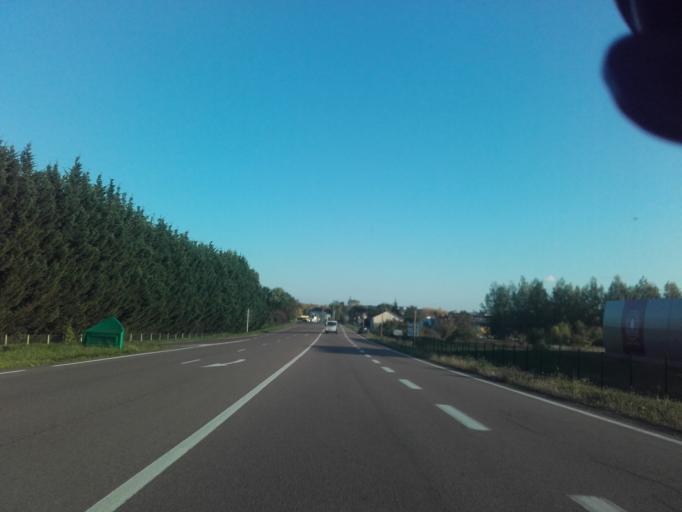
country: FR
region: Bourgogne
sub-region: Departement de la Cote-d'Or
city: Corpeau
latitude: 46.9242
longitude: 4.7447
